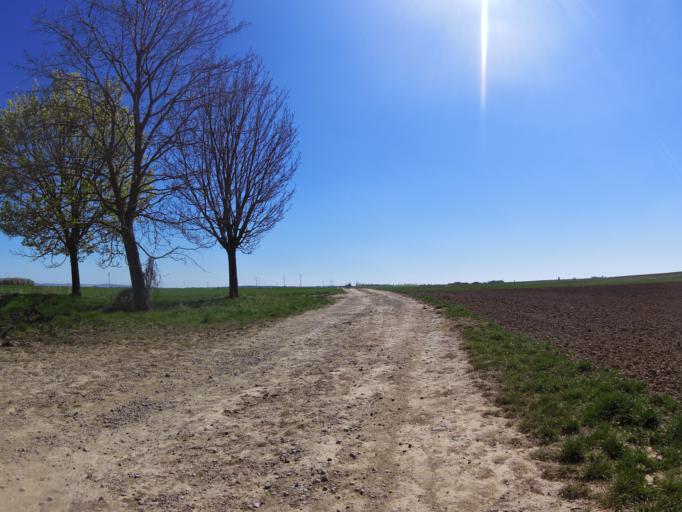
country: DE
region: Bavaria
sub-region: Regierungsbezirk Unterfranken
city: Biebelried
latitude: 49.8131
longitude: 10.0934
